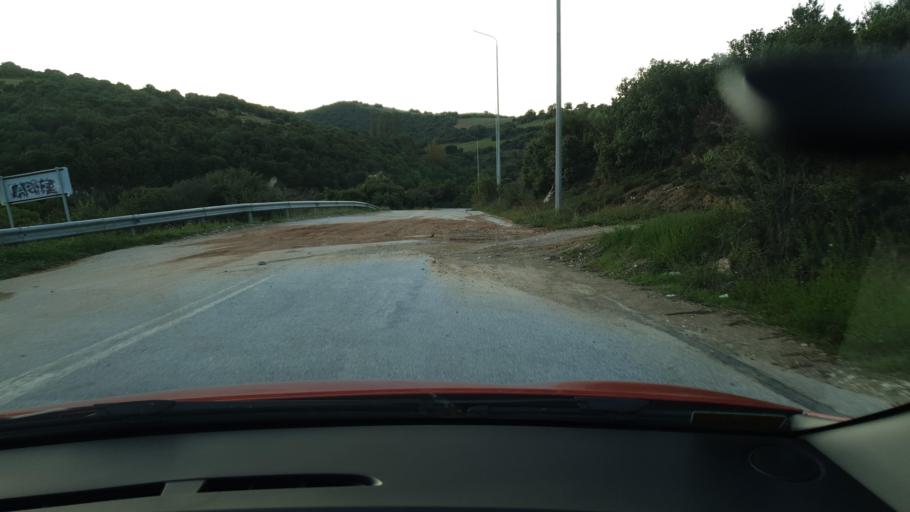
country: GR
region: Central Macedonia
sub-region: Nomos Chalkidikis
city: Galatista
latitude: 40.4617
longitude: 23.3233
